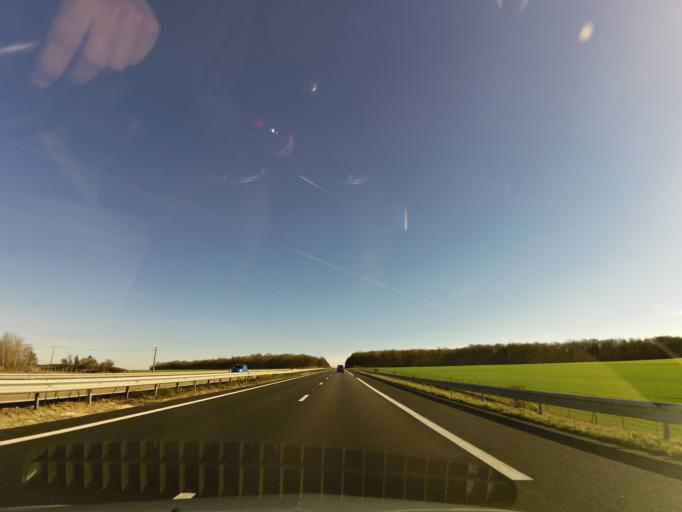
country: FR
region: Bourgogne
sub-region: Departement de l'Yonne
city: Vermenton
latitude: 47.7135
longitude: 3.7749
